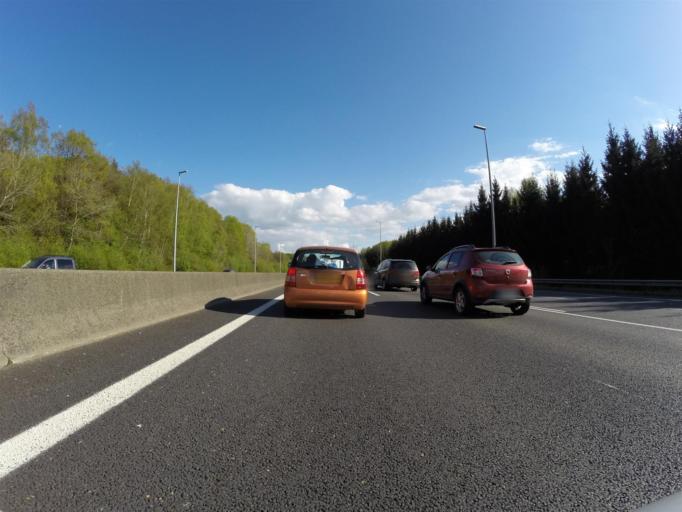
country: LU
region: Luxembourg
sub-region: Canton de Luxembourg
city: Hesperange
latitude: 49.5693
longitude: 6.1264
